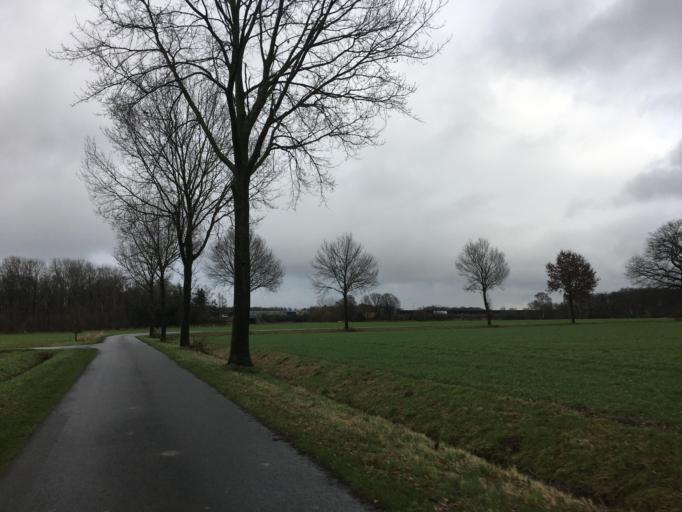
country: DE
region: North Rhine-Westphalia
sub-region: Regierungsbezirk Munster
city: Muenster
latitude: 51.9321
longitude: 7.5470
